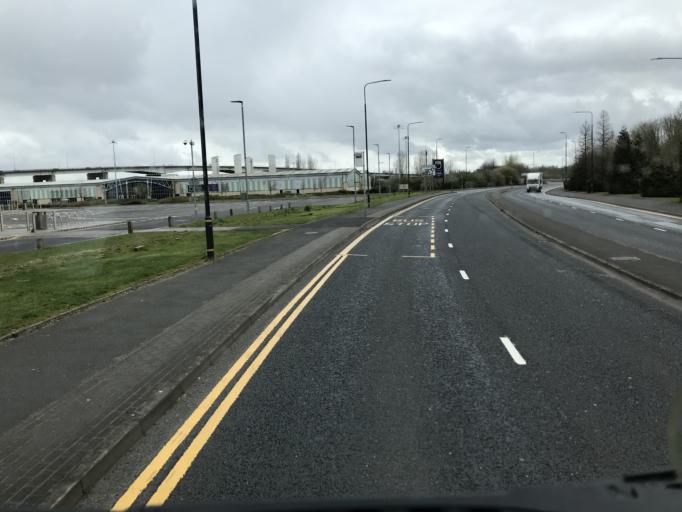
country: GB
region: England
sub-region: Trafford
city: Urmston
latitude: 53.4689
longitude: -2.3608
